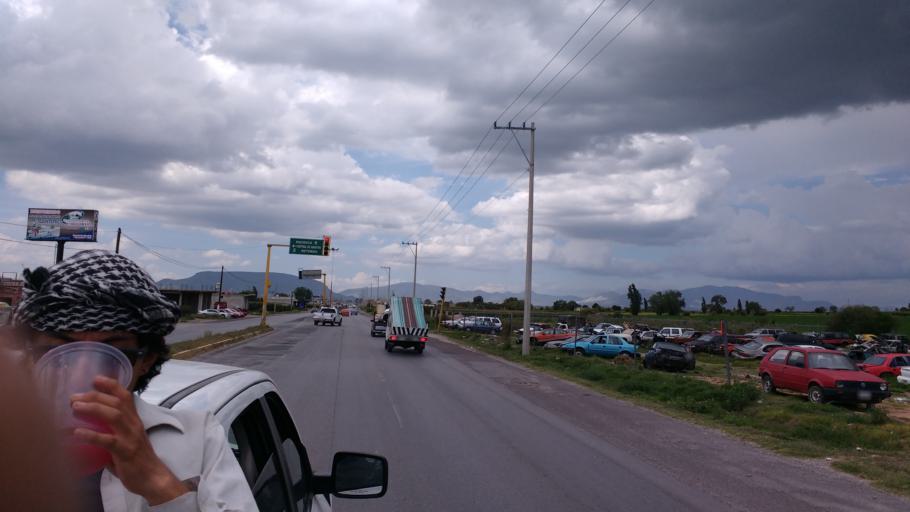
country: MX
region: Hidalgo
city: Tlahuelilpan
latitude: 20.1478
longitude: -99.2347
